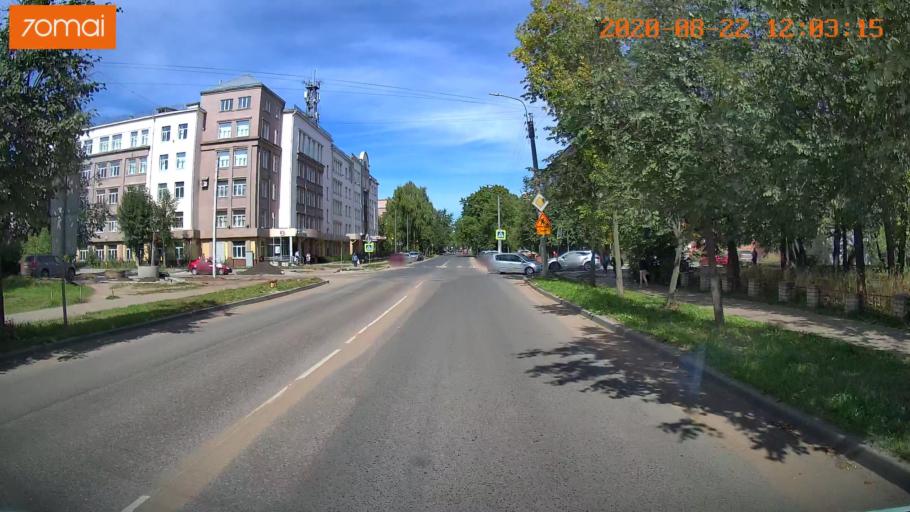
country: RU
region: Ivanovo
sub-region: Gorod Ivanovo
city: Ivanovo
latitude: 57.0079
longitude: 40.9799
